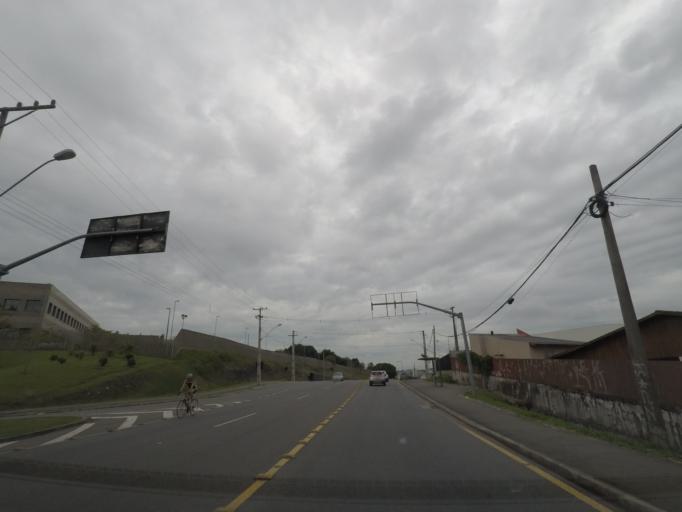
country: BR
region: Parana
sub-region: Curitiba
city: Curitiba
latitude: -25.4457
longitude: -49.2457
